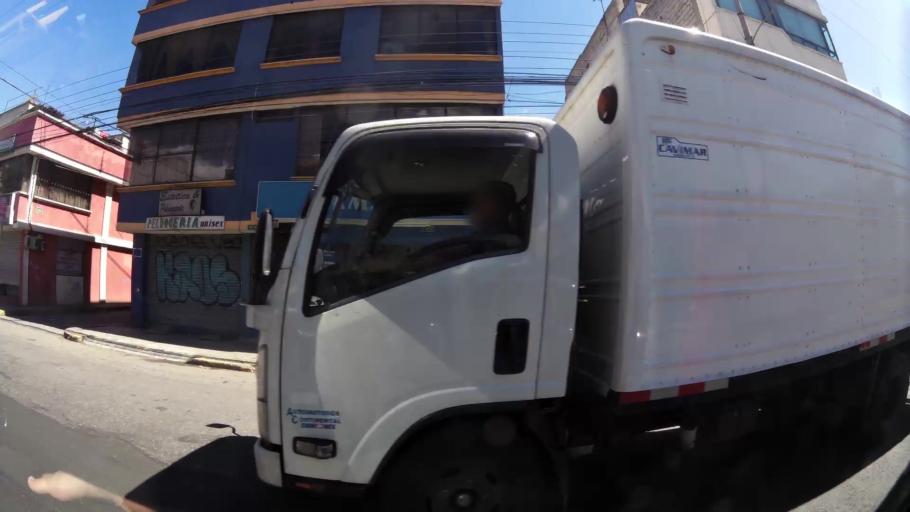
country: EC
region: Pichincha
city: Quito
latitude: -0.2671
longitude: -78.5452
